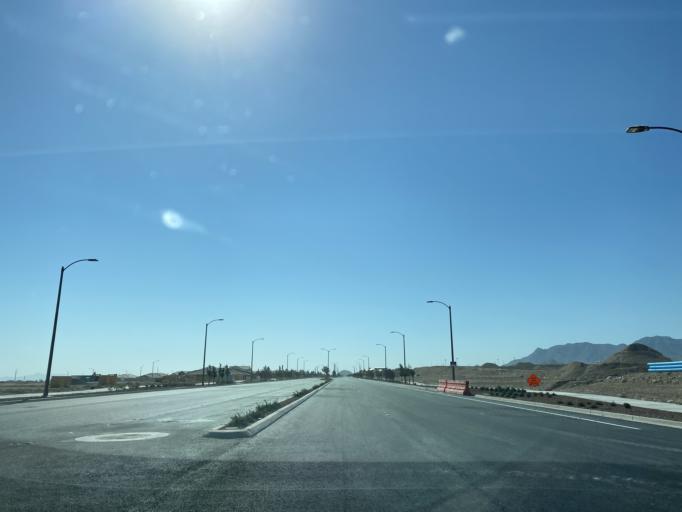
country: US
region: Nevada
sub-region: Clark County
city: Summerlin South
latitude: 36.3194
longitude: -115.3148
